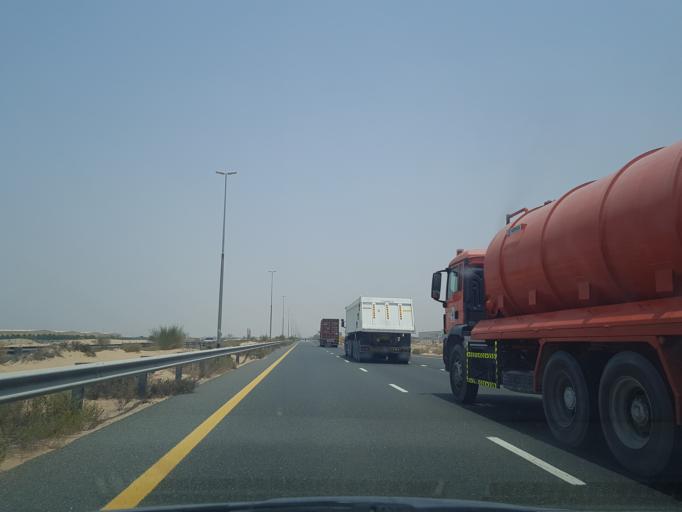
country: AE
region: Ash Shariqah
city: Sharjah
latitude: 25.1450
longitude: 55.4353
